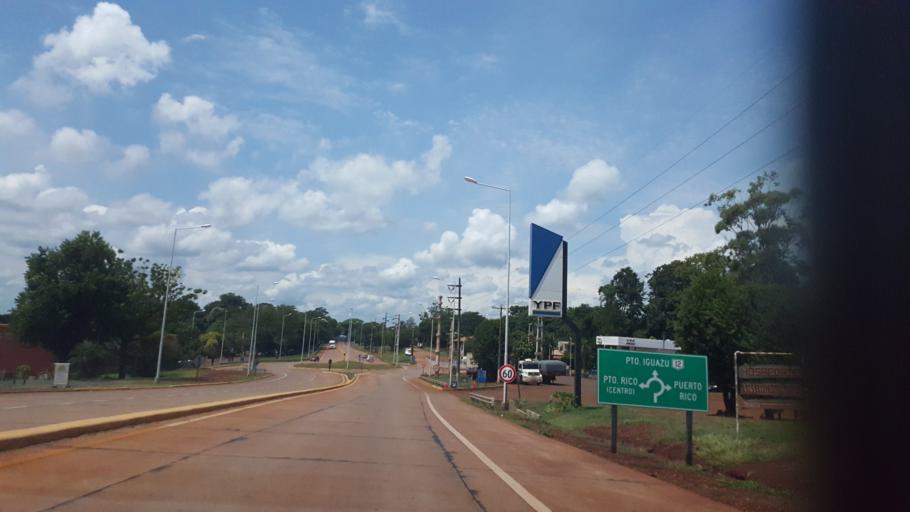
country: AR
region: Misiones
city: Puerto Rico
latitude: -26.8208
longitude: -55.0243
